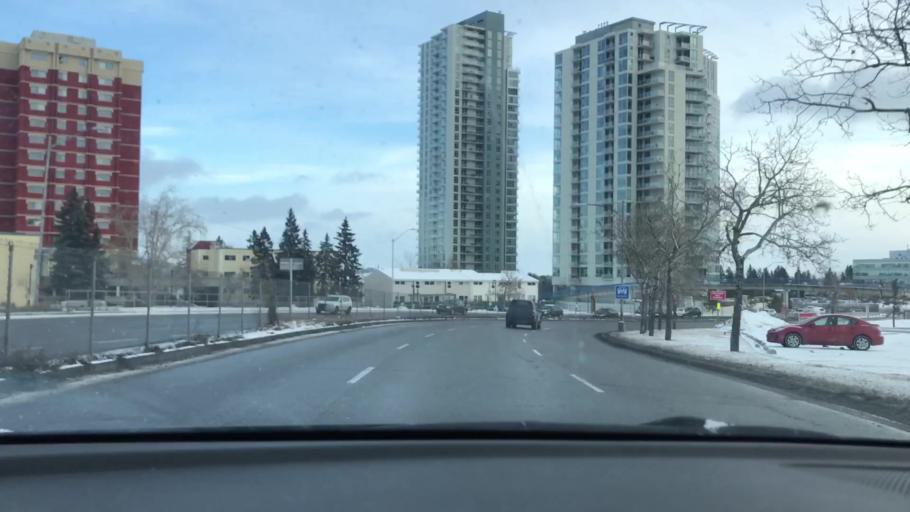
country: CA
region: Alberta
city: Calgary
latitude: 51.0445
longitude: -114.1397
